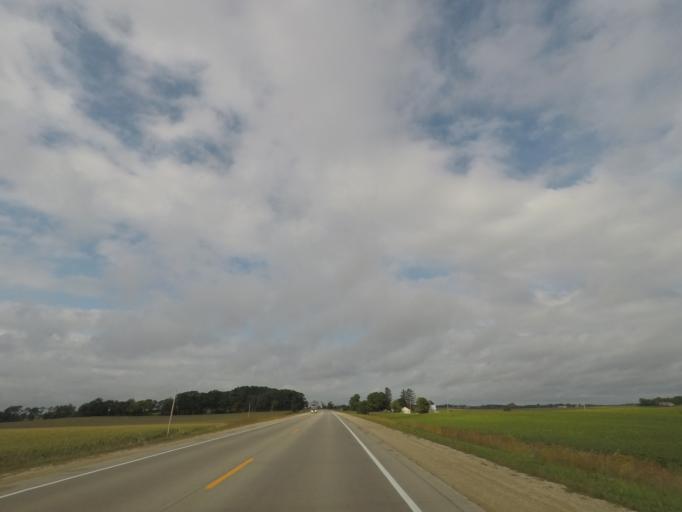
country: US
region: Wisconsin
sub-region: Dane County
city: Deerfield
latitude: 43.0356
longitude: -89.1178
